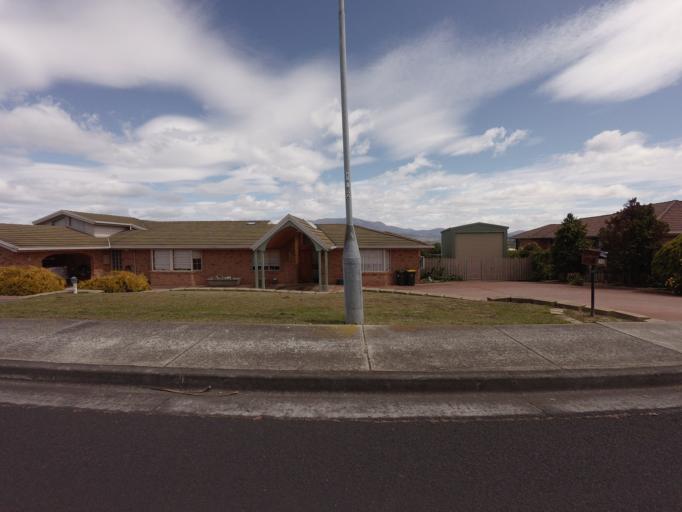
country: AU
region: Tasmania
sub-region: Clarence
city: Howrah
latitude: -42.8862
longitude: 147.4092
